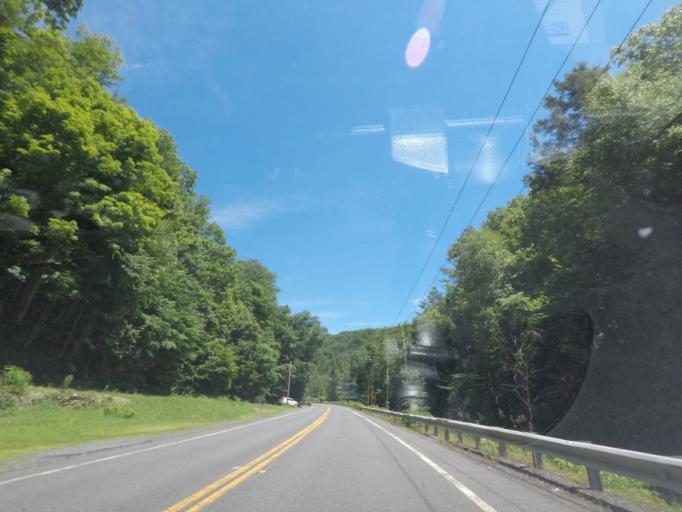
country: US
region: Massachusetts
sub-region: Berkshire County
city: Becket
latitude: 42.2699
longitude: -73.0041
